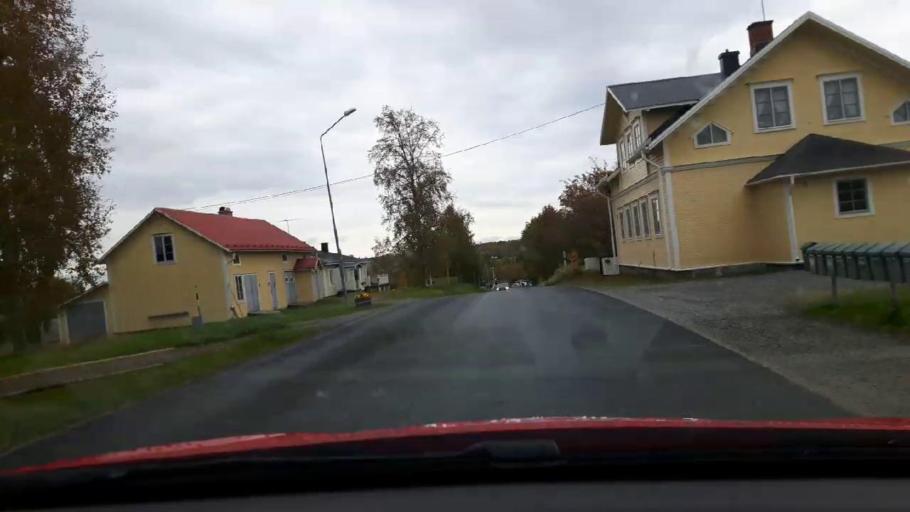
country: SE
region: Jaemtland
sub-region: Bergs Kommun
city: Hoverberg
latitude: 62.9180
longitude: 14.5204
